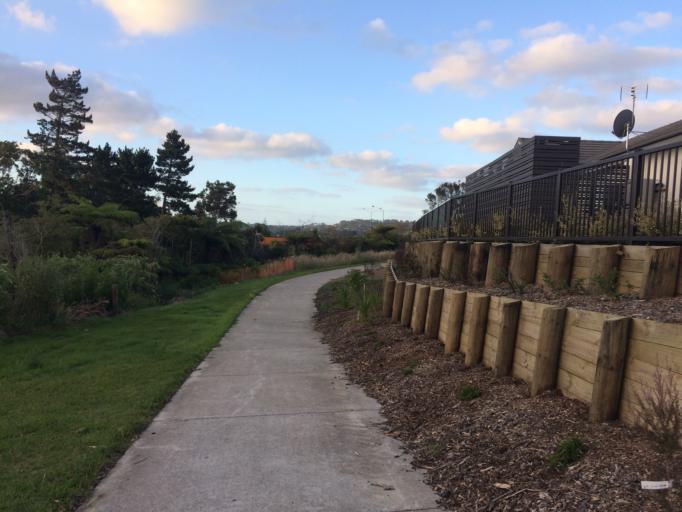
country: NZ
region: Auckland
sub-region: Auckland
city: Rosebank
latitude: -36.7901
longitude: 174.6584
